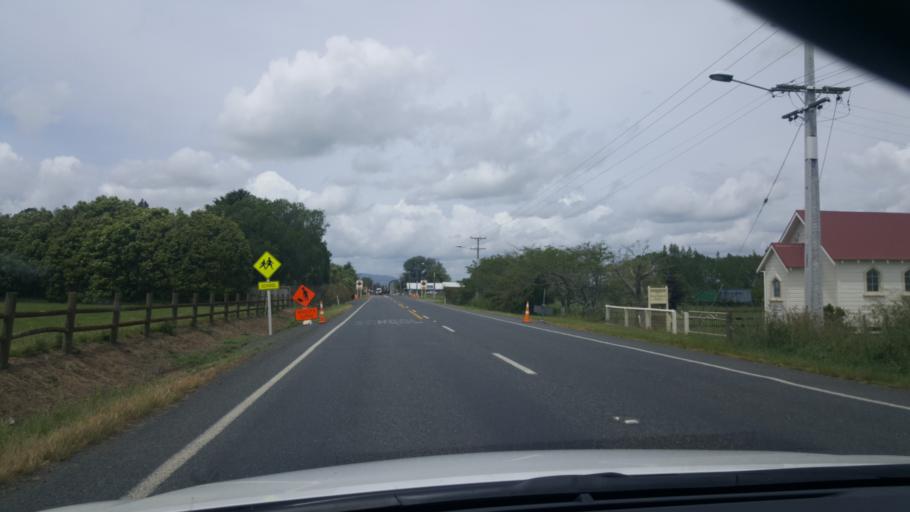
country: NZ
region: Waikato
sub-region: Matamata-Piako District
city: Matamata
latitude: -37.8802
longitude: 175.7564
